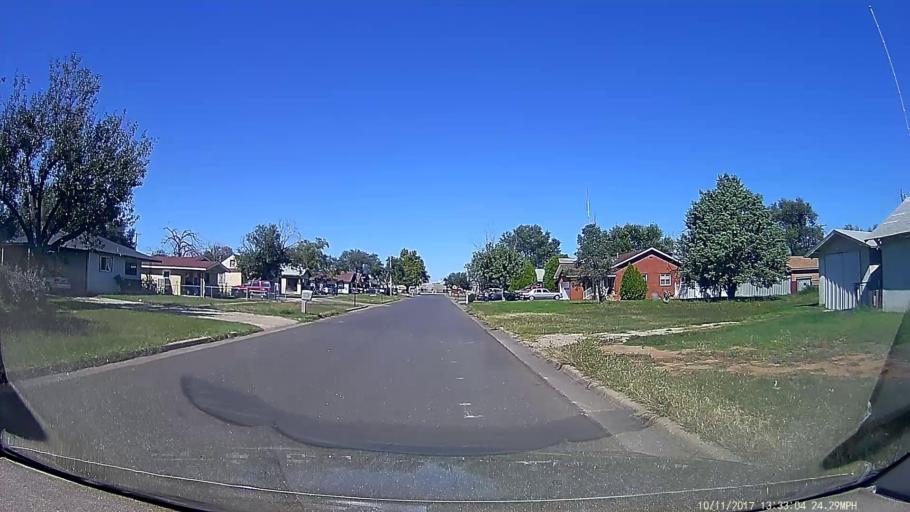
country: US
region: New Mexico
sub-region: Curry County
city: Clovis
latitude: 34.4111
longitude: -103.2104
